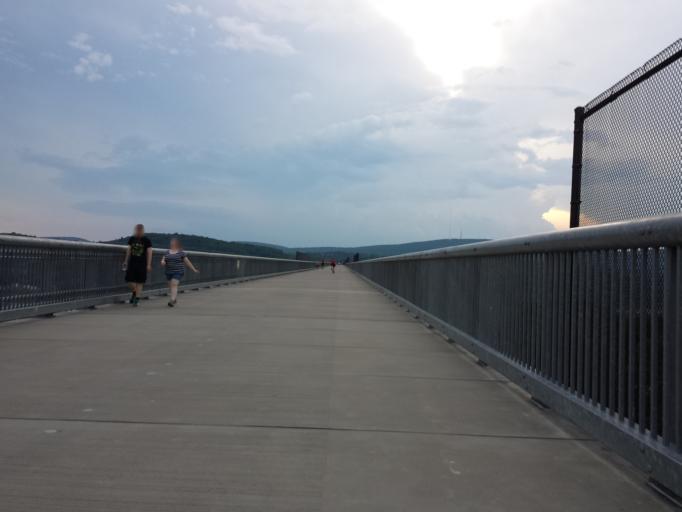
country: US
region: New York
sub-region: Dutchess County
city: Poughkeepsie
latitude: 41.7105
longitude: -73.9340
